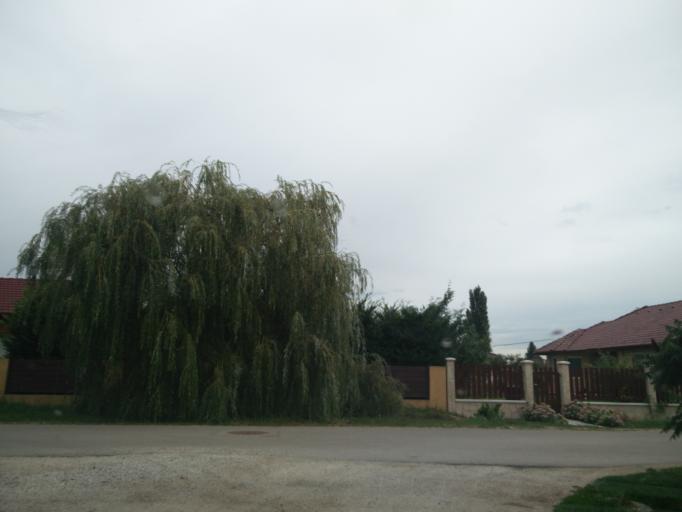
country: HU
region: Fejer
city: Gardony
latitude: 47.2161
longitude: 18.6388
